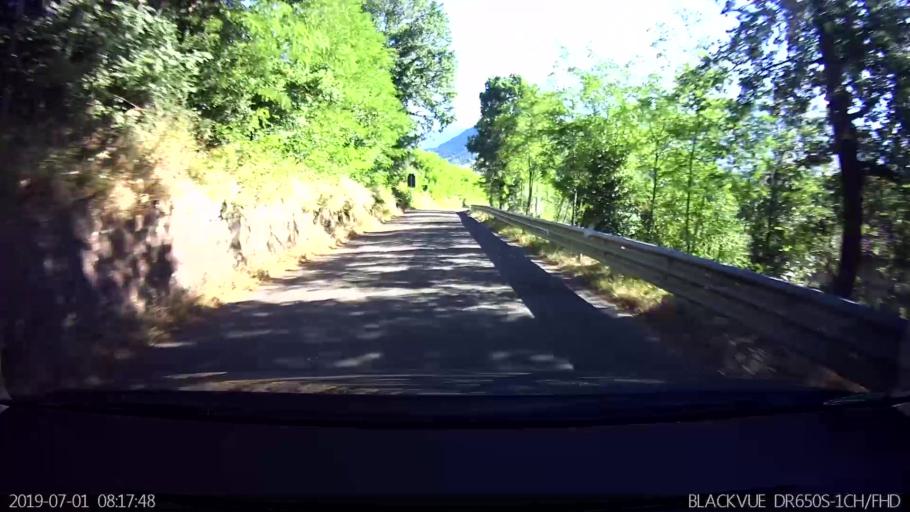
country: IT
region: Latium
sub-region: Provincia di Frosinone
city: Veroli
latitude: 41.7089
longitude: 13.4401
